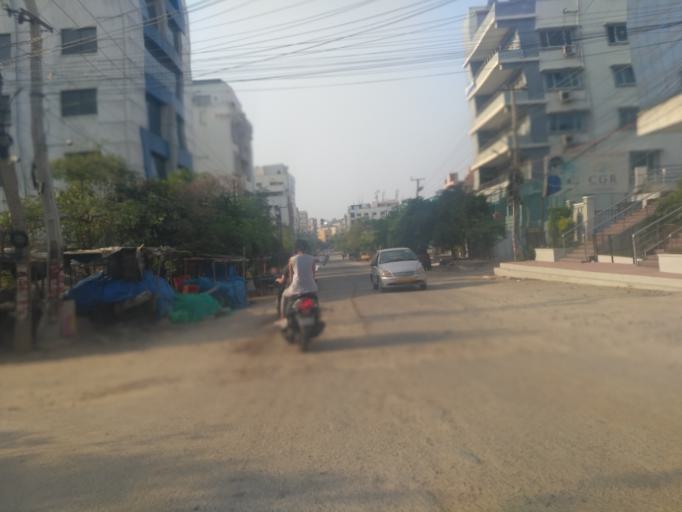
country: IN
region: Telangana
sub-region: Rangareddi
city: Kukatpalli
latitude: 17.4487
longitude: 78.3920
